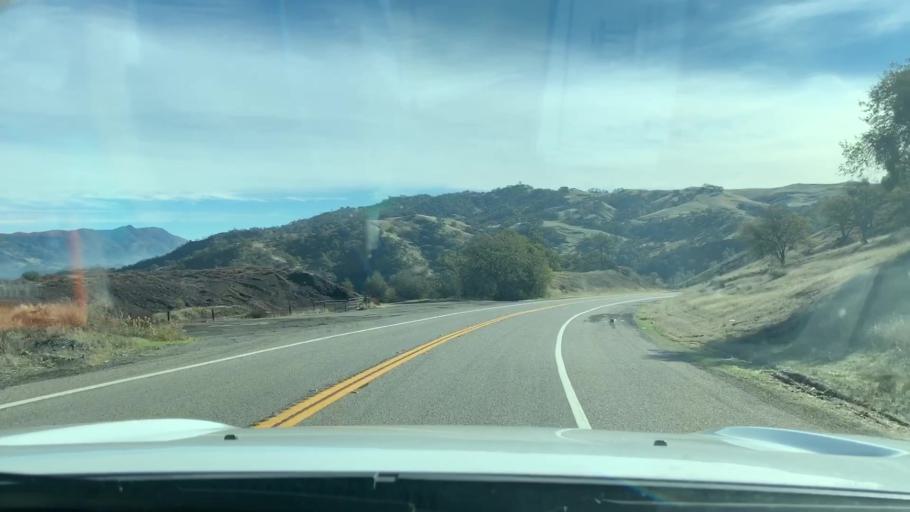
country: US
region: California
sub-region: Monterey County
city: King City
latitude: 36.1928
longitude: -120.7586
